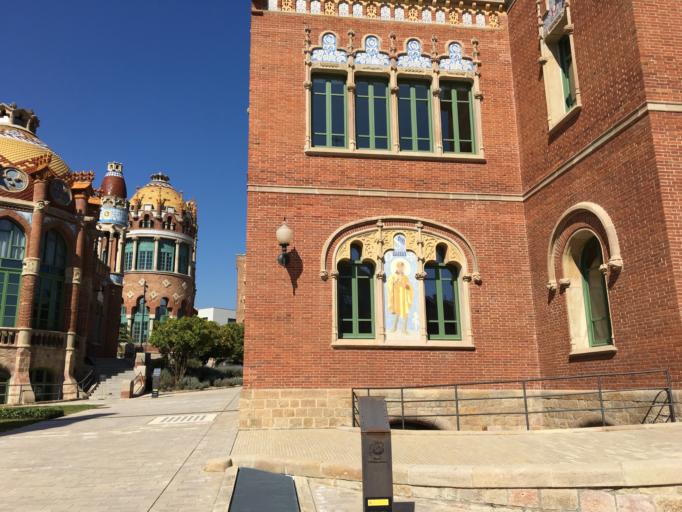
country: ES
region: Catalonia
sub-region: Provincia de Barcelona
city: Horta-Guinardo
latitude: 41.4126
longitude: 2.1742
